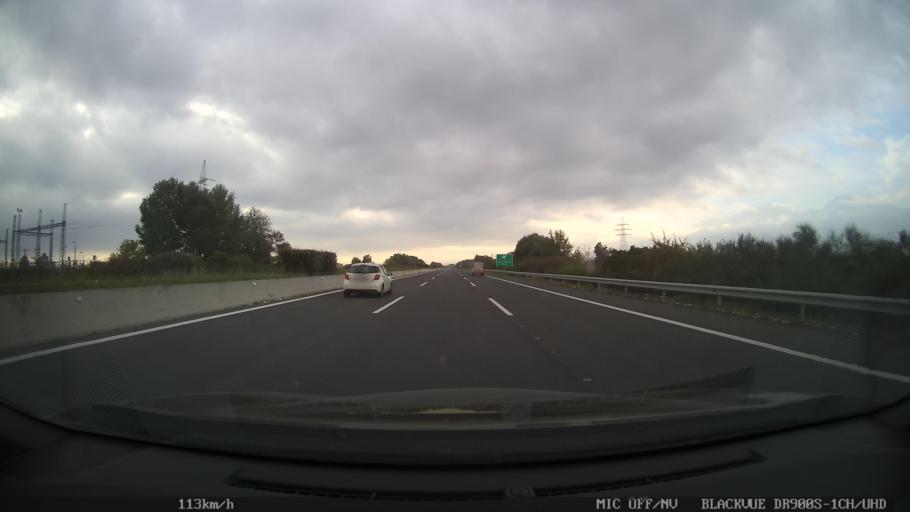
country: GR
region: Central Macedonia
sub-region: Nomos Pierias
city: Nea Efesos
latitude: 40.2164
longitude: 22.5426
